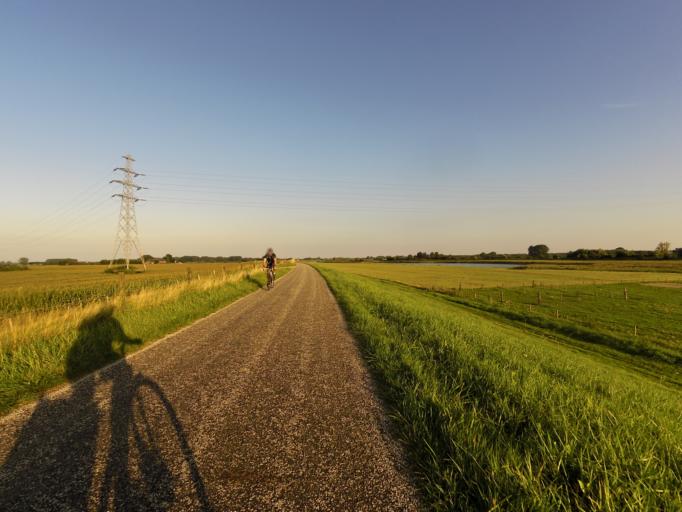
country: NL
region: Gelderland
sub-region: Gemeente Duiven
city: Duiven
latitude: 51.9101
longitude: 6.0016
